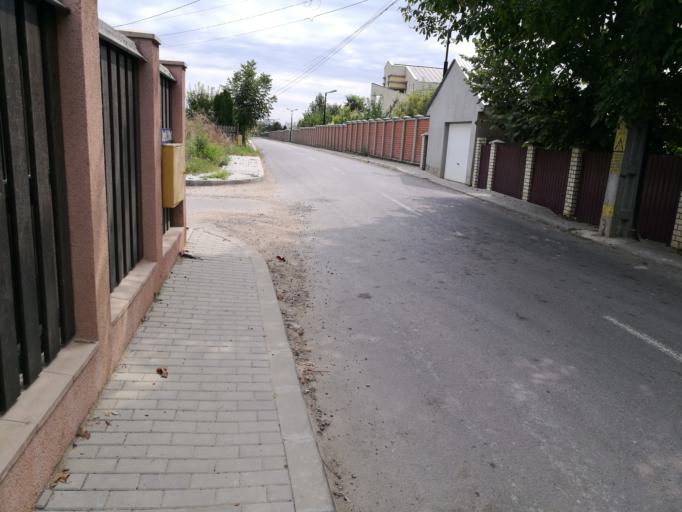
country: RO
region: Iasi
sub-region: Comuna Valea Lupului
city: Valea Lupului
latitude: 47.1755
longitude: 27.5230
